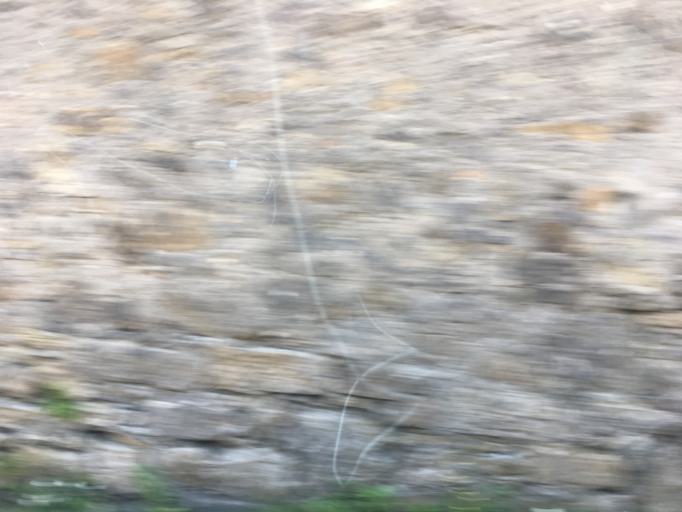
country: PT
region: Lisbon
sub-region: Sintra
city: Sintra
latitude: 38.8055
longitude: -9.3802
